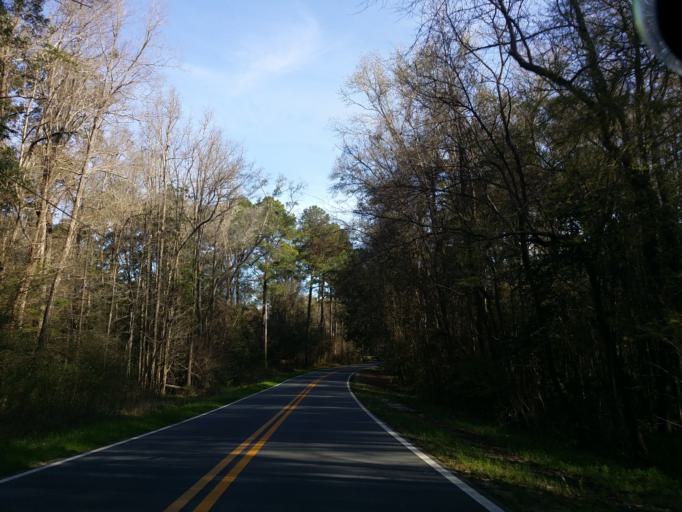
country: US
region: Florida
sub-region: Leon County
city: Tallahassee
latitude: 30.4104
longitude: -84.1595
